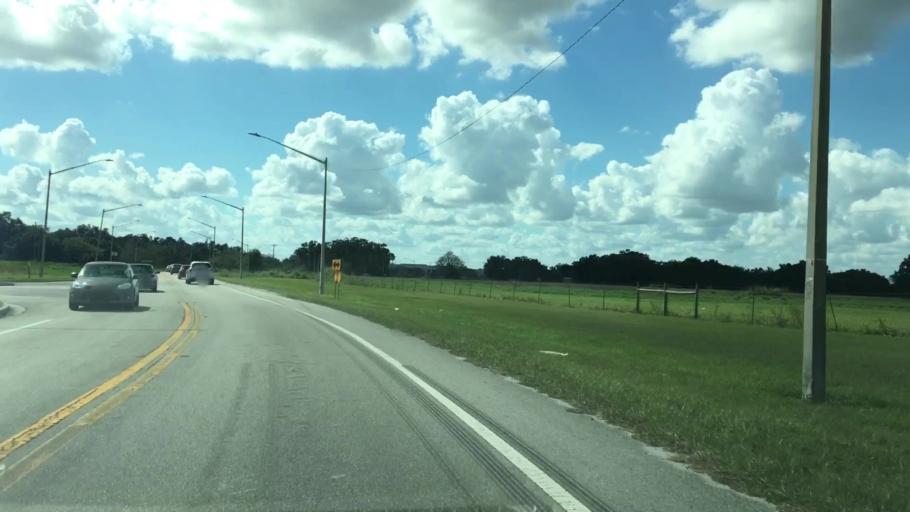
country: US
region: Florida
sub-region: Orange County
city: Conway
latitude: 28.4676
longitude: -81.3201
